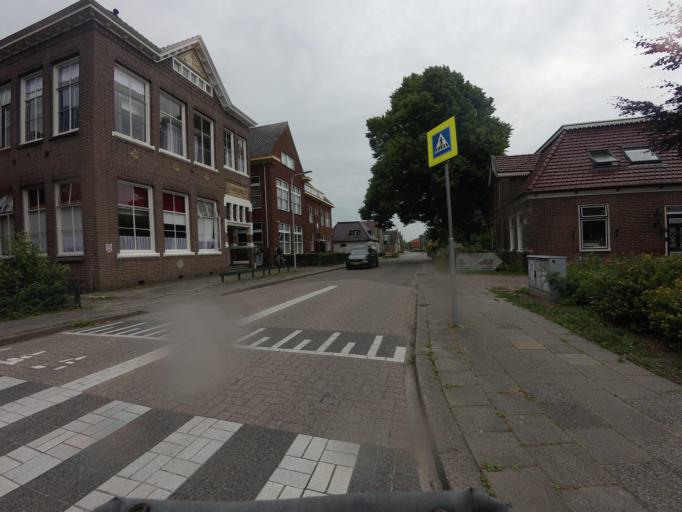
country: NL
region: North Holland
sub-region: Gemeente Enkhuizen
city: Enkhuizen
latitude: 52.6979
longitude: 5.2178
